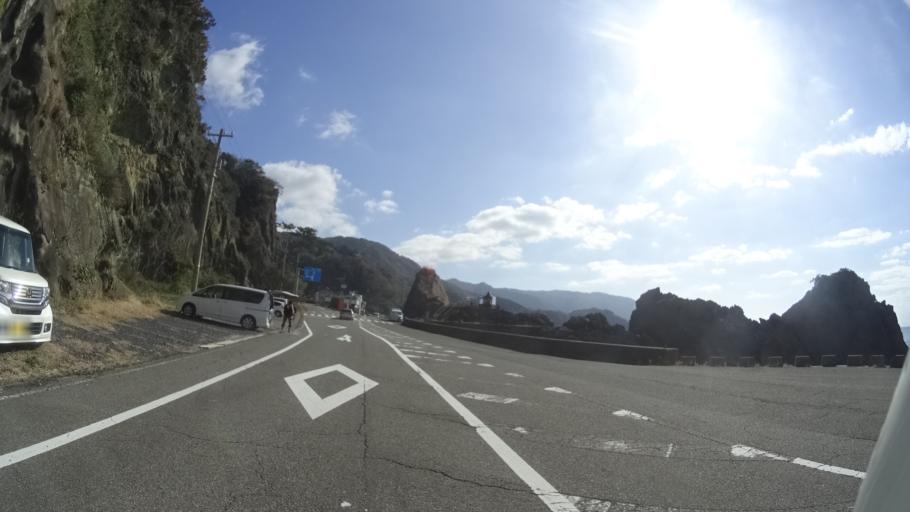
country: JP
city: Asahi
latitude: 35.9568
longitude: 135.9782
